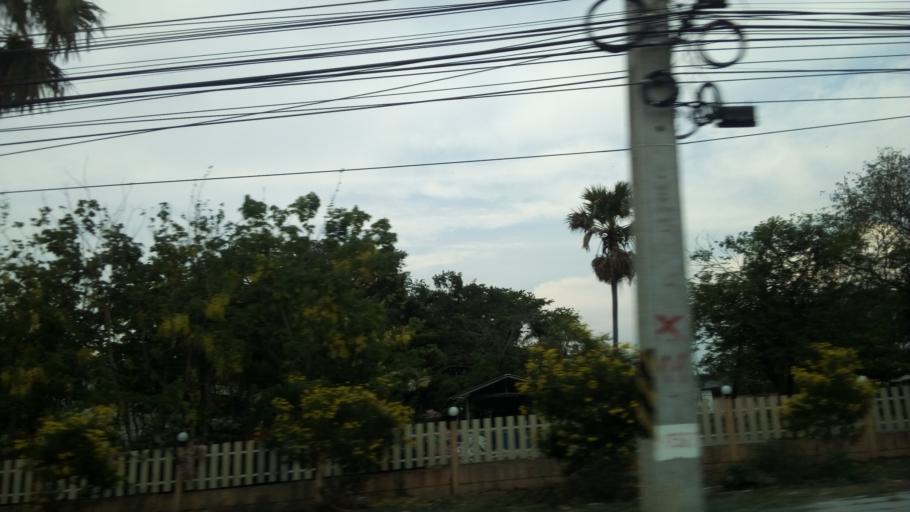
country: TH
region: Pathum Thani
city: Thanyaburi
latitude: 14.0275
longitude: 100.7101
